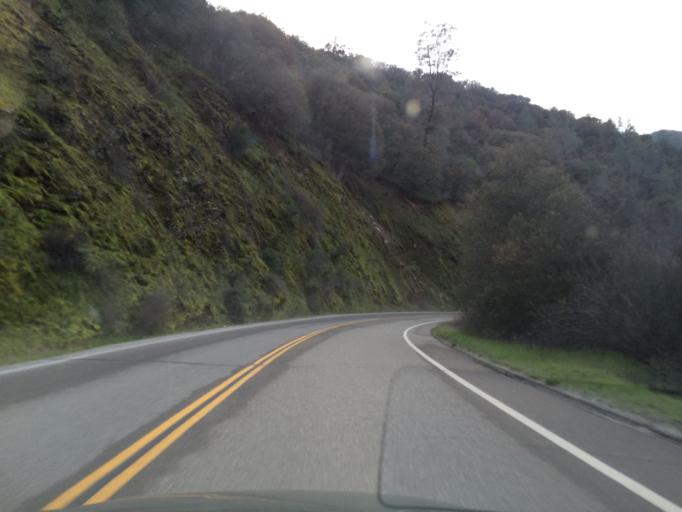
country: US
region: California
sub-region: Mariposa County
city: Midpines
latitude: 37.6008
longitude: -119.9619
